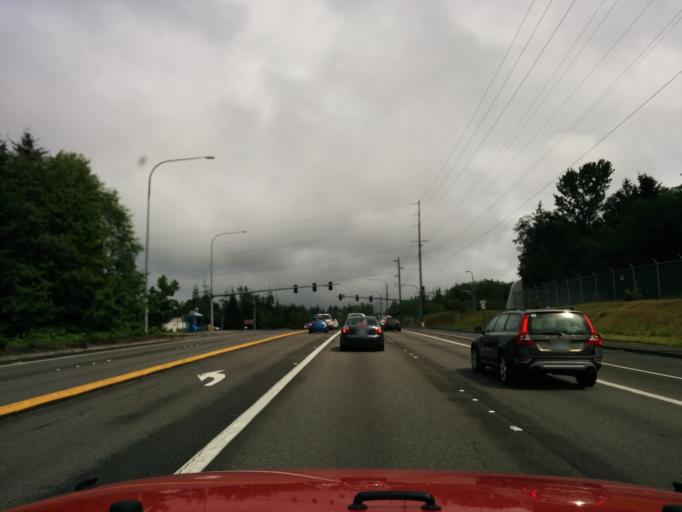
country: US
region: Washington
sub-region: Snohomish County
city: Mukilteo
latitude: 47.9041
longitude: -122.2930
